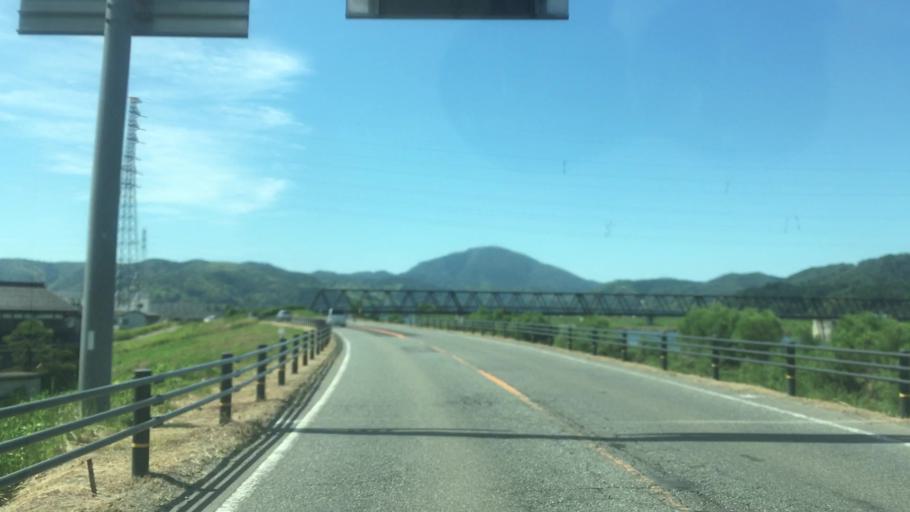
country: JP
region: Hyogo
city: Toyooka
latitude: 35.5509
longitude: 134.8242
